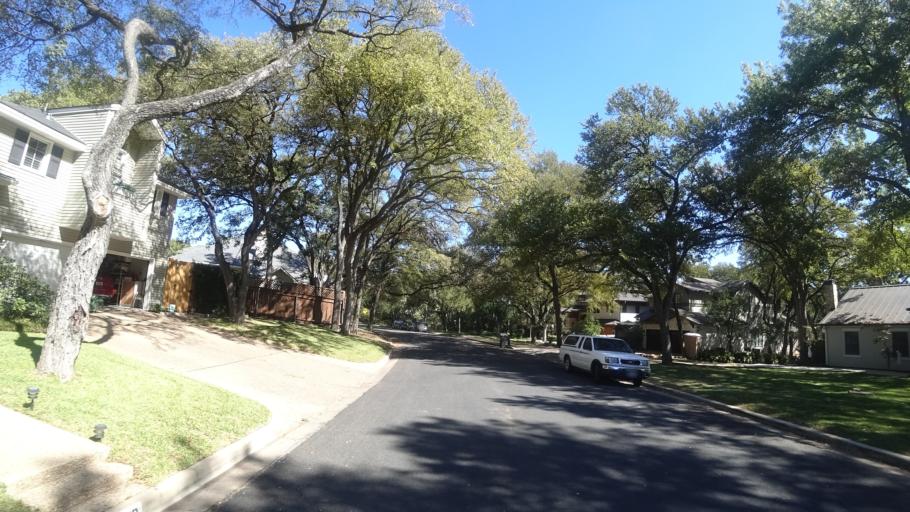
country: US
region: Texas
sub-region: Travis County
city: Rollingwood
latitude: 30.2919
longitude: -97.7643
